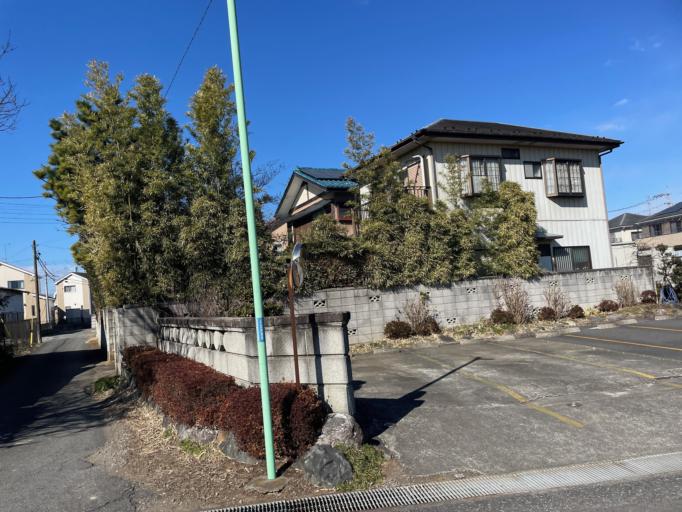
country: JP
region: Saitama
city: Kawagoe
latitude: 35.9434
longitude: 139.4659
